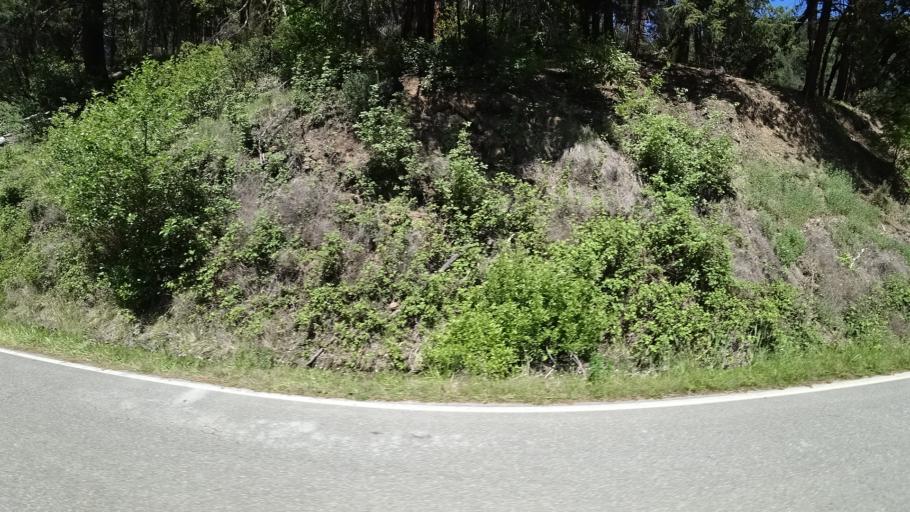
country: US
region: California
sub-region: Trinity County
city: Hayfork
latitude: 40.7476
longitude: -123.2715
